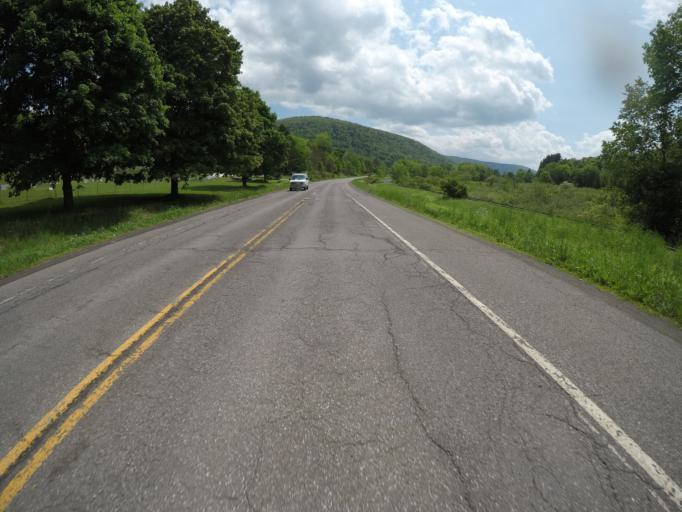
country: US
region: New York
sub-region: Delaware County
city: Stamford
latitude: 42.1867
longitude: -74.5983
